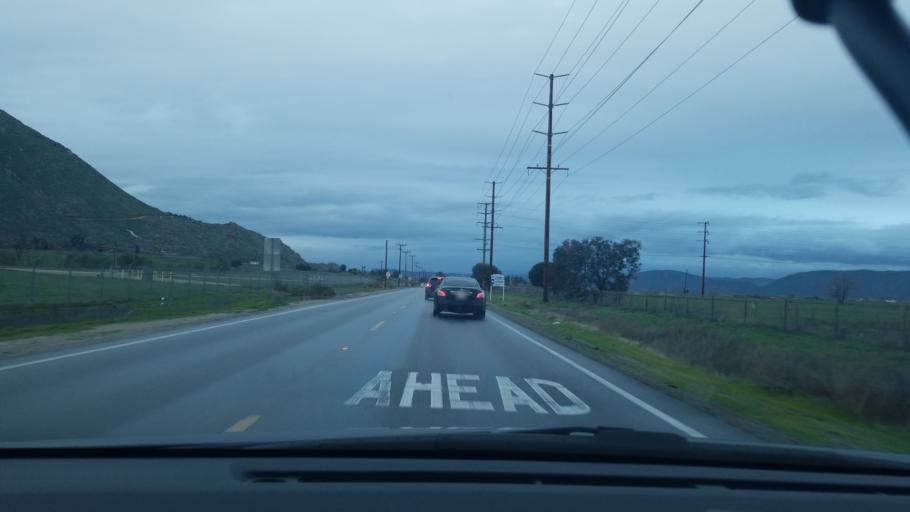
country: US
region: California
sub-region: Riverside County
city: Green Acres
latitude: 33.7711
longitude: -117.0334
